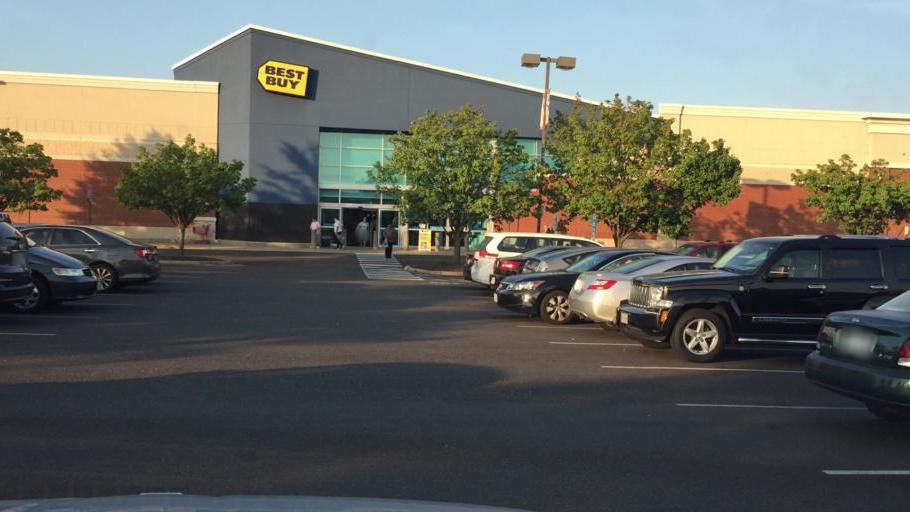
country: US
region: Virginia
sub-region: Fairfax County
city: Baileys Crossroads
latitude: 38.8502
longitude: -77.1321
